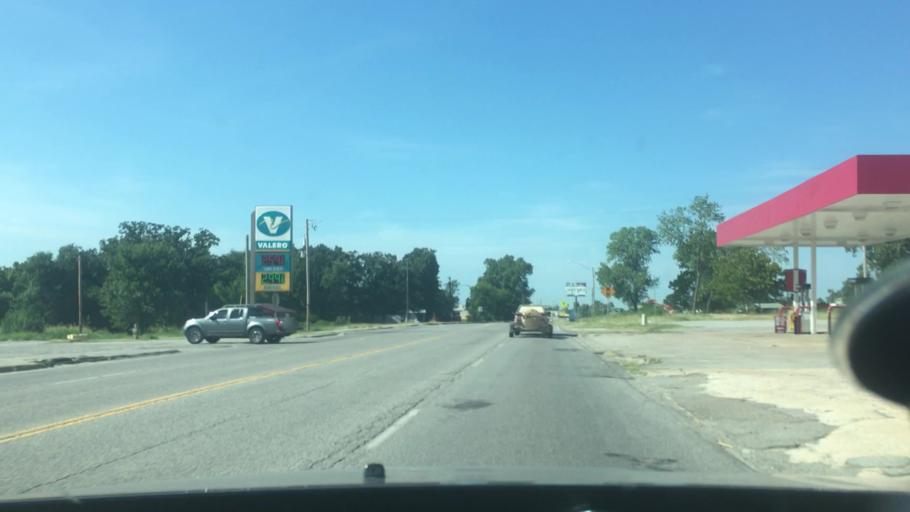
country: US
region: Oklahoma
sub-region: Atoka County
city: Atoka
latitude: 34.3201
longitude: -96.1673
